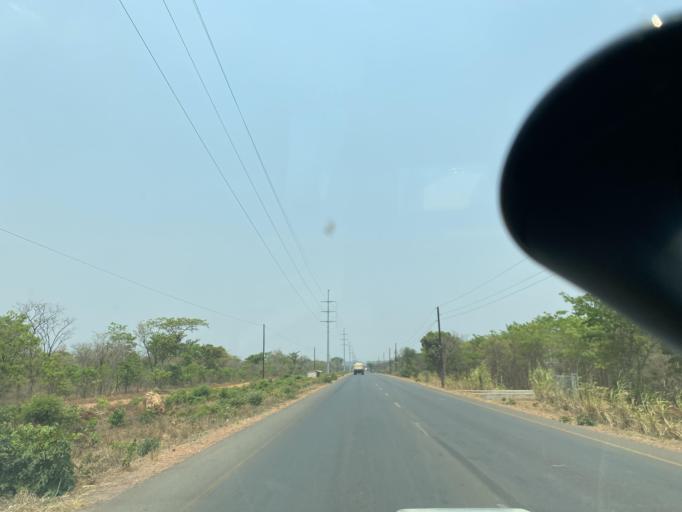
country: ZM
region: Lusaka
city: Lusaka
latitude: -15.5127
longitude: 28.4511
